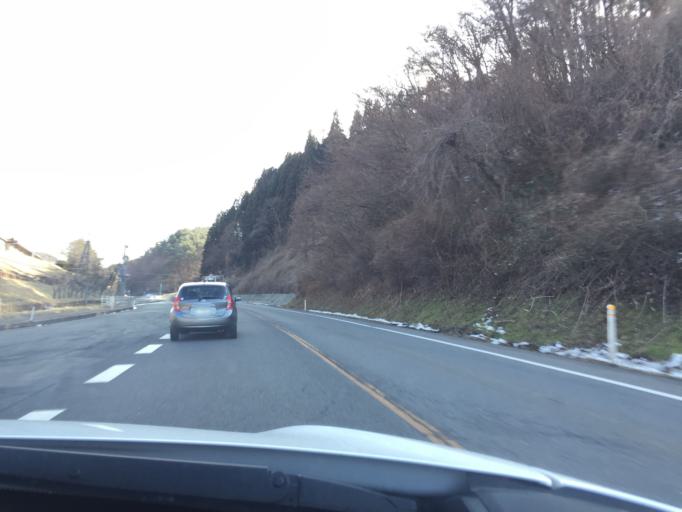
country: JP
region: Fukushima
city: Ishikawa
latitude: 37.1763
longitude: 140.6498
